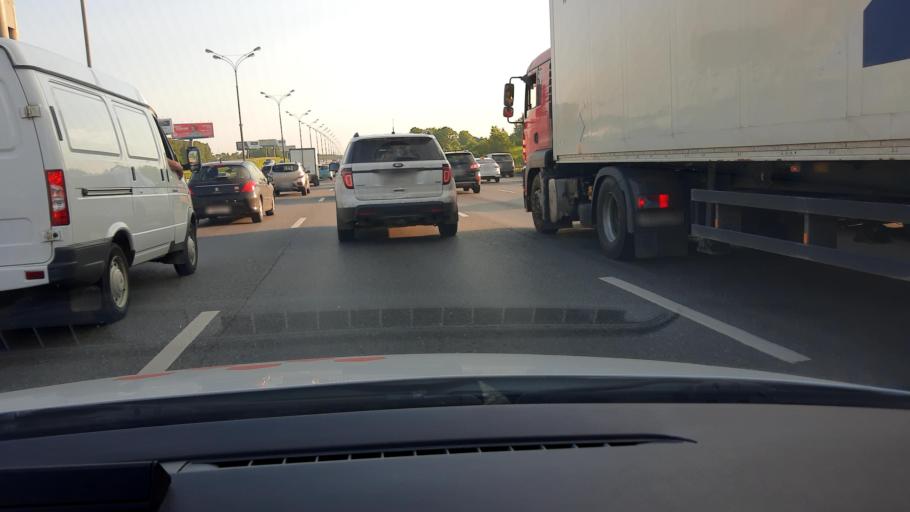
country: RU
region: Moscow
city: Zyablikovo
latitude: 55.6136
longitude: 37.7733
